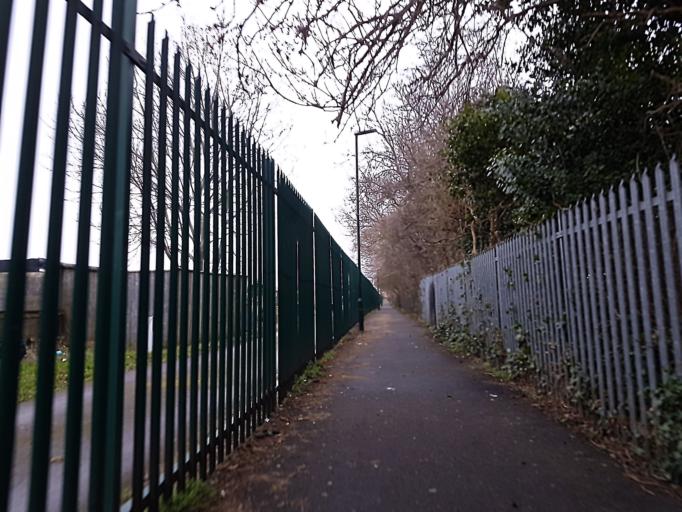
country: GB
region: England
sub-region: North East Lincolnshire
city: Grimbsy
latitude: 53.5598
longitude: -0.1030
